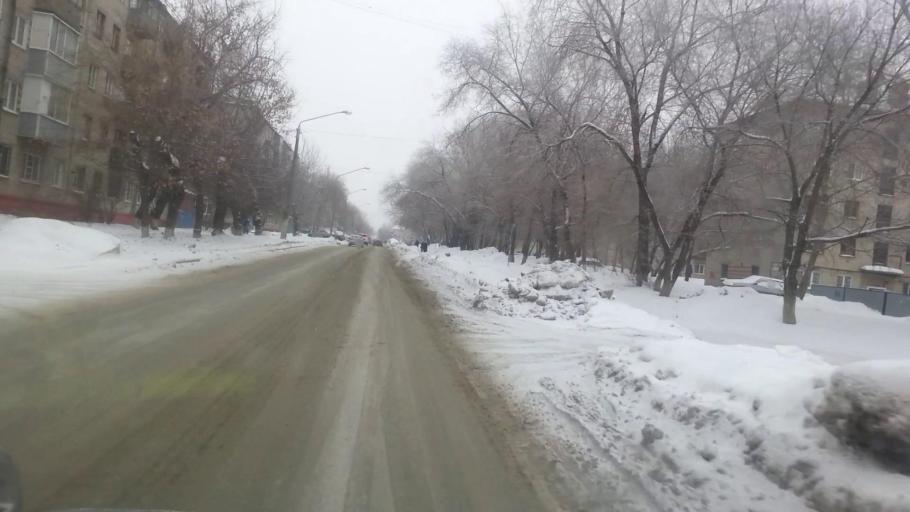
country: RU
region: Altai Krai
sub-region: Gorod Barnaulskiy
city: Barnaul
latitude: 53.3793
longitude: 83.7188
